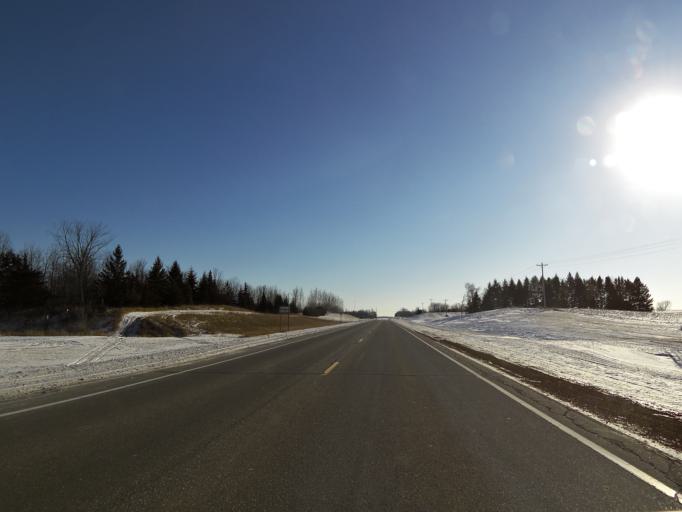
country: US
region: Minnesota
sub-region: Le Sueur County
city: New Prague
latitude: 44.5892
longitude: -93.5070
